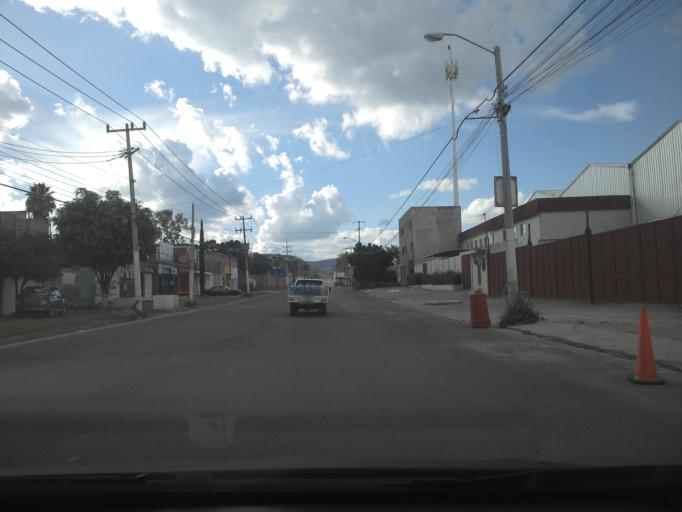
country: MX
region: Jalisco
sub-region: Tlajomulco de Zuniga
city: Palomar
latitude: 20.6149
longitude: -103.4390
